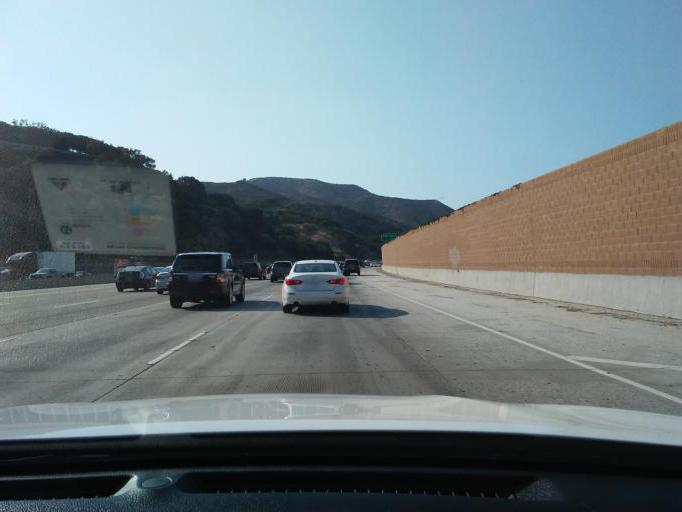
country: US
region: California
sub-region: Los Angeles County
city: Westwood, Los Angeles
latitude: 34.0807
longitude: -118.4729
